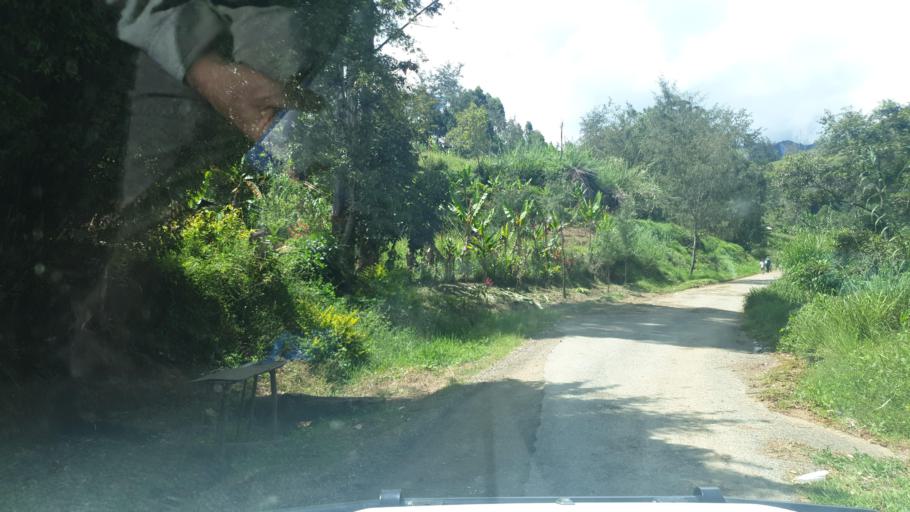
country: PG
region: Chimbu
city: Kundiawa
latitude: -6.1451
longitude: 145.1330
